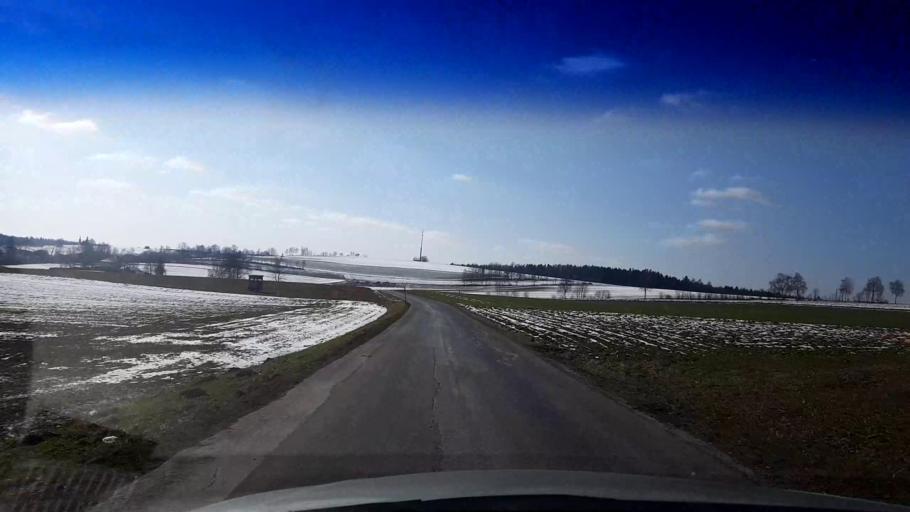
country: DE
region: Bavaria
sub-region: Upper Palatinate
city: Waldsassen
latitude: 50.0447
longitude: 12.2887
